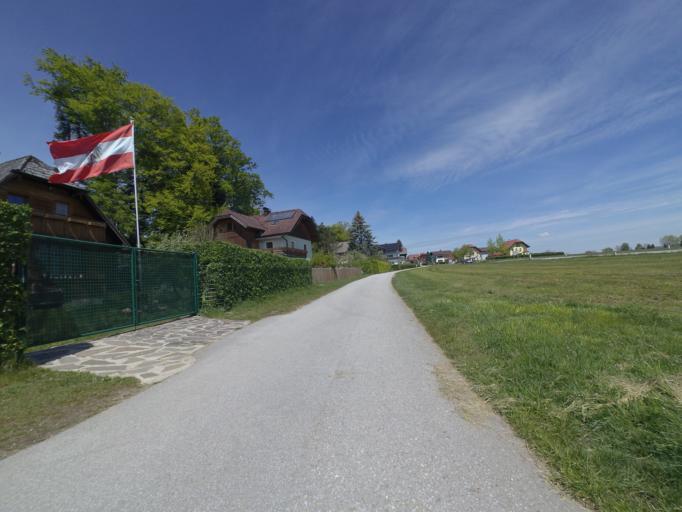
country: AT
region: Salzburg
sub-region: Politischer Bezirk Salzburg-Umgebung
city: Seeham
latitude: 47.9564
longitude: 13.0734
